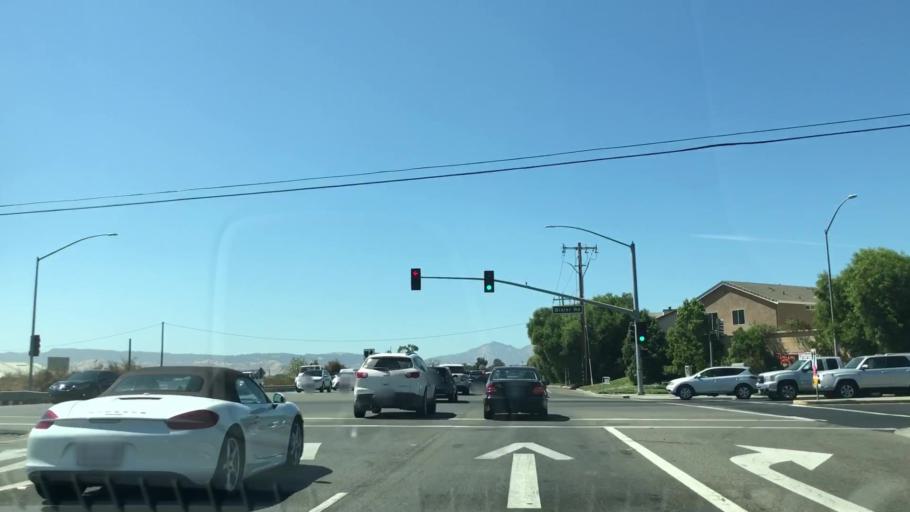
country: US
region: California
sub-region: Contra Costa County
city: Byron
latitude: 37.8895
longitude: -121.6227
